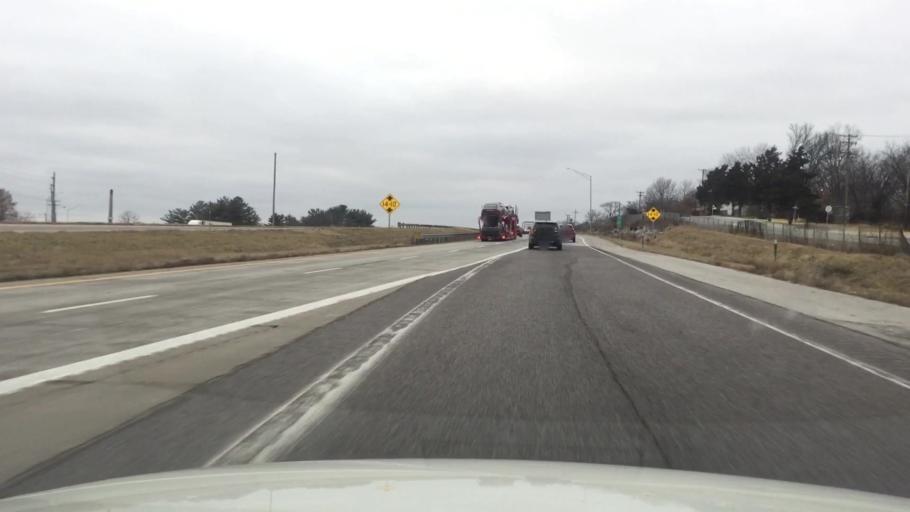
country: US
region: Missouri
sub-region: Boone County
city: Columbia
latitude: 38.9637
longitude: -92.2981
